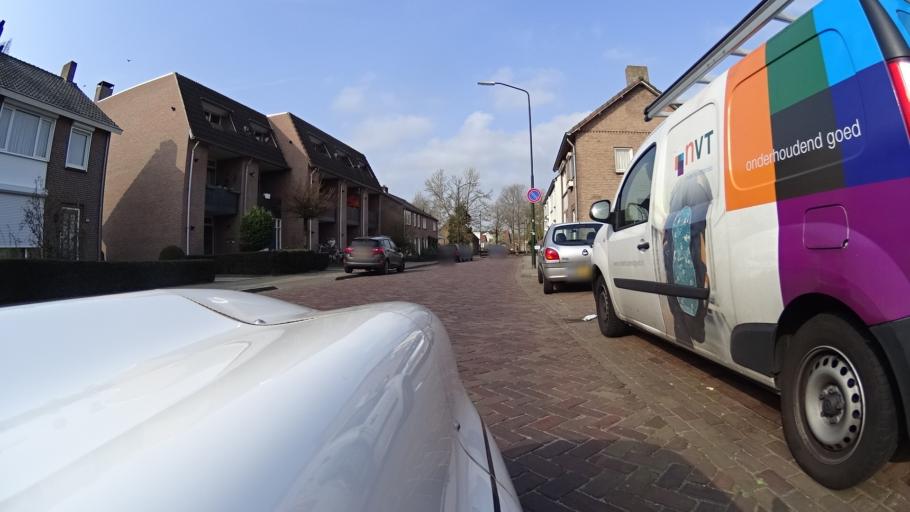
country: NL
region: North Brabant
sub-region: Gemeente Boekel
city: Boekel
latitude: 51.5536
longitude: 5.6907
